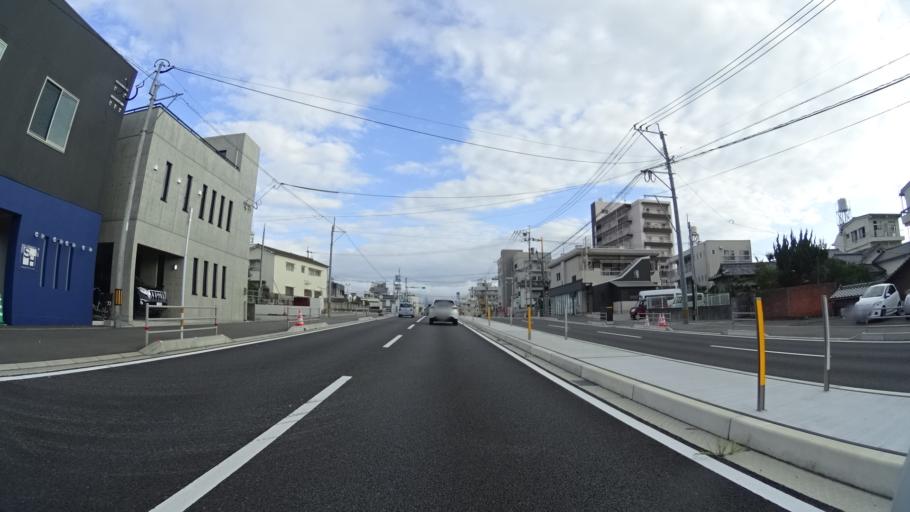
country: JP
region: Oita
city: Beppu
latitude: 33.2826
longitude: 131.4970
